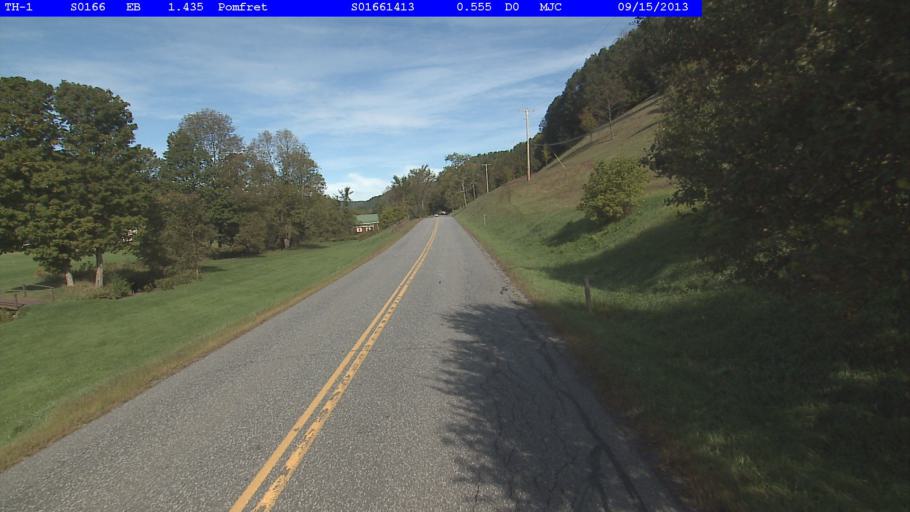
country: US
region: Vermont
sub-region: Windsor County
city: Woodstock
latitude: 43.6581
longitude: -72.5314
